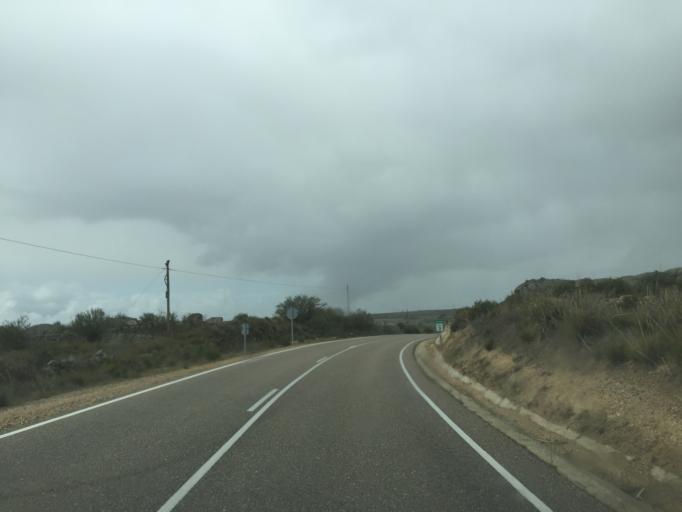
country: ES
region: Castille and Leon
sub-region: Provincia de Zamora
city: Villalcampo
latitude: 41.5265
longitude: -6.0201
